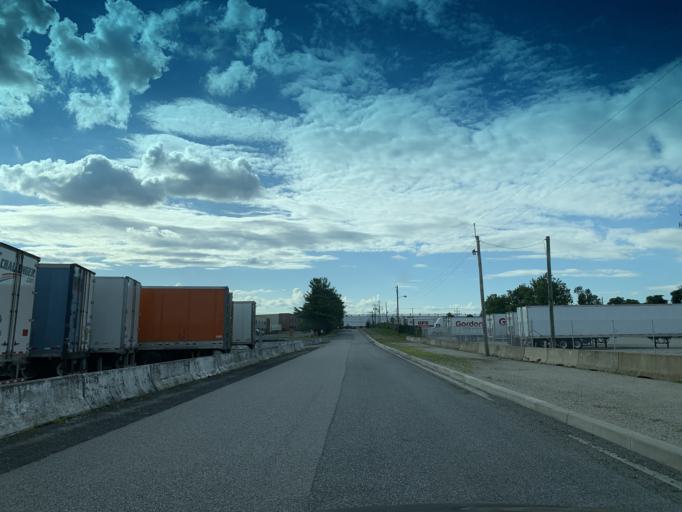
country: US
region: Maryland
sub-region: Harford County
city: Perryman
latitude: 39.4868
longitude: -76.1826
